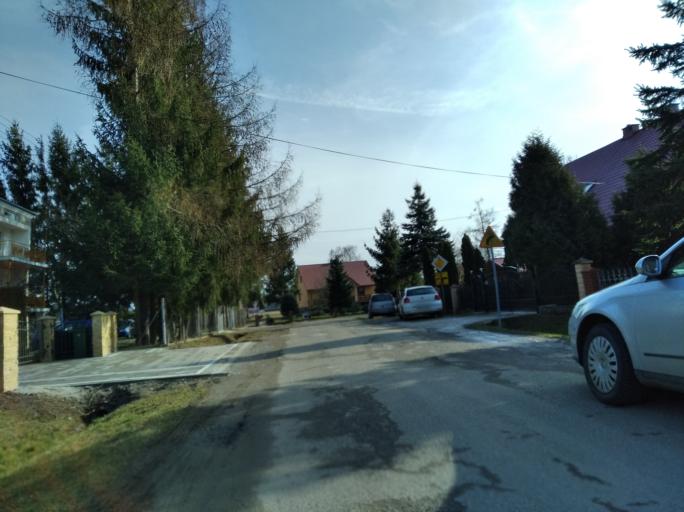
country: PL
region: Subcarpathian Voivodeship
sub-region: Powiat brzozowski
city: Humniska
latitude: 49.6685
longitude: 22.0543
